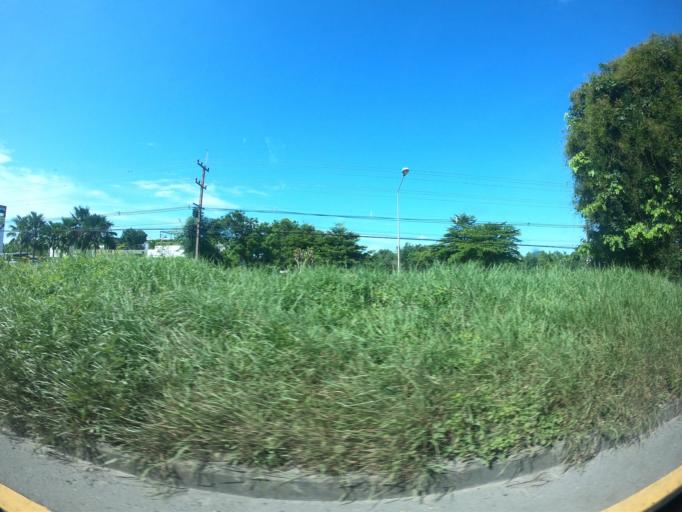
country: TH
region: Nakhon Nayok
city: Ban Na
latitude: 14.2417
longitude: 101.1189
